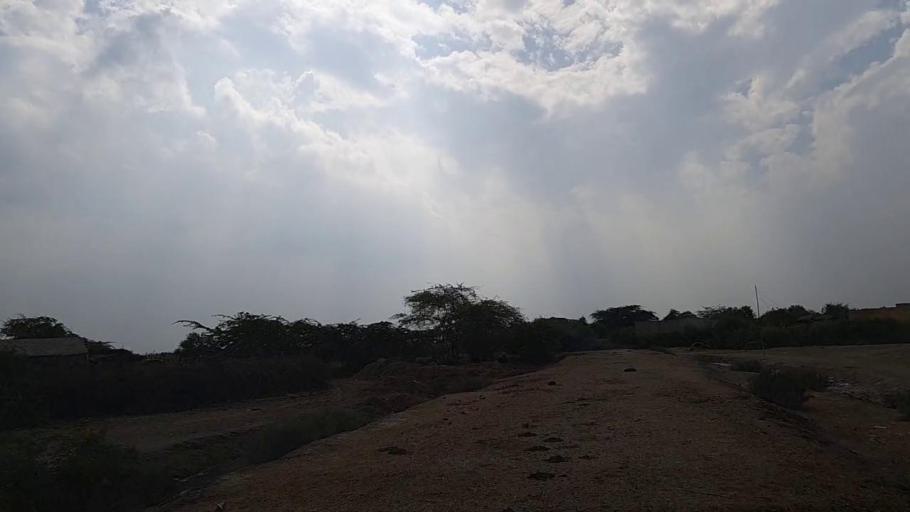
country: PK
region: Sindh
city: Daro Mehar
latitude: 24.7196
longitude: 68.1368
